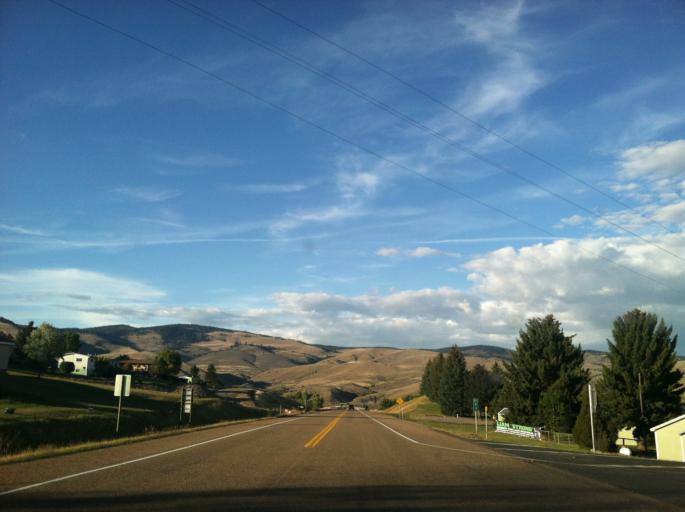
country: US
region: Montana
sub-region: Granite County
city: Philipsburg
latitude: 46.6590
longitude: -113.1582
